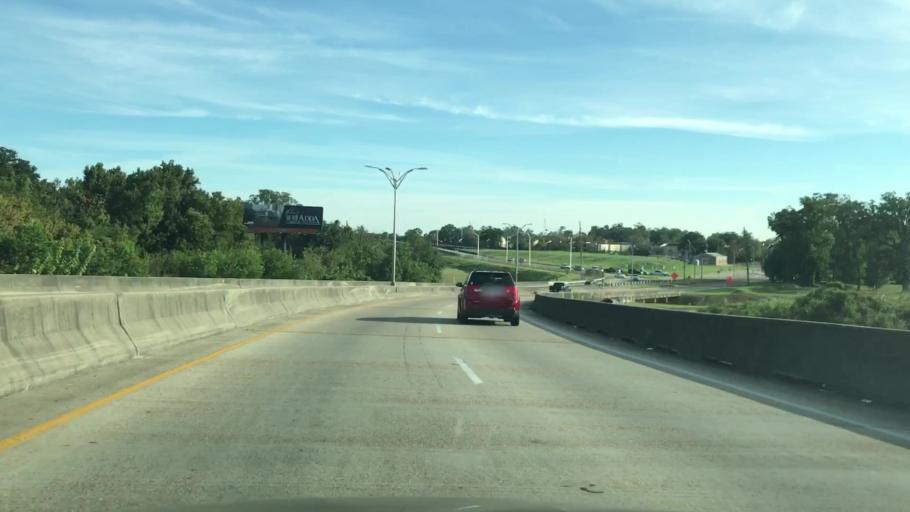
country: US
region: Louisiana
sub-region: Jefferson Parish
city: River Ridge
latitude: 29.9727
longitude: -90.2051
